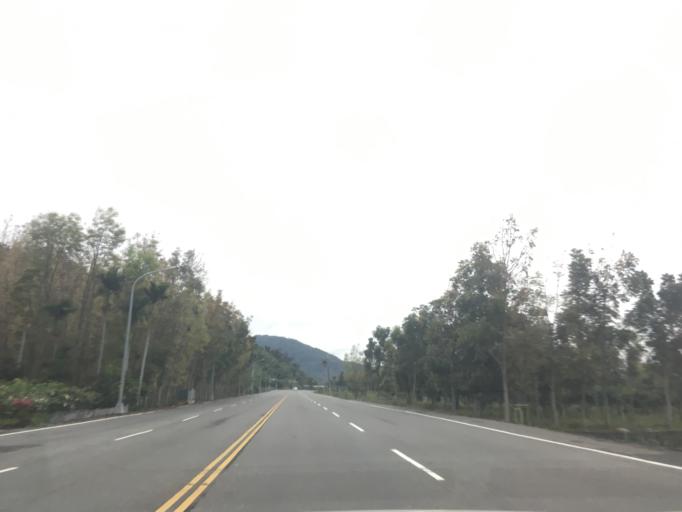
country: TW
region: Taiwan
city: Taitung City
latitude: 22.7362
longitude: 121.0566
